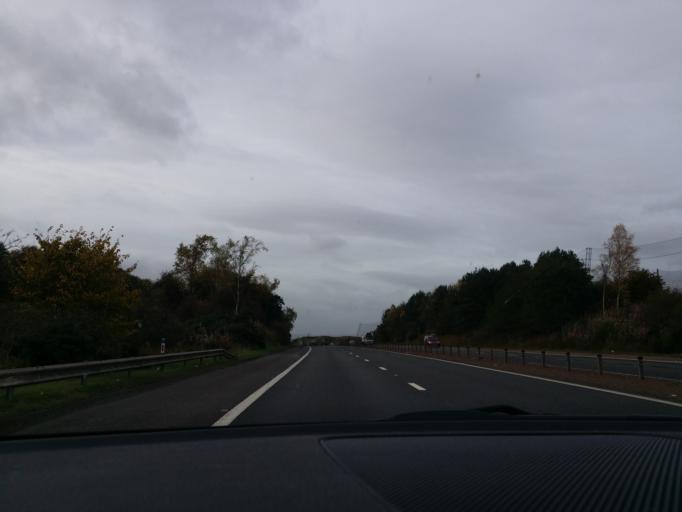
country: GB
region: Scotland
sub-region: Falkirk
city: Polmont
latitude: 55.9872
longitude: -3.6673
